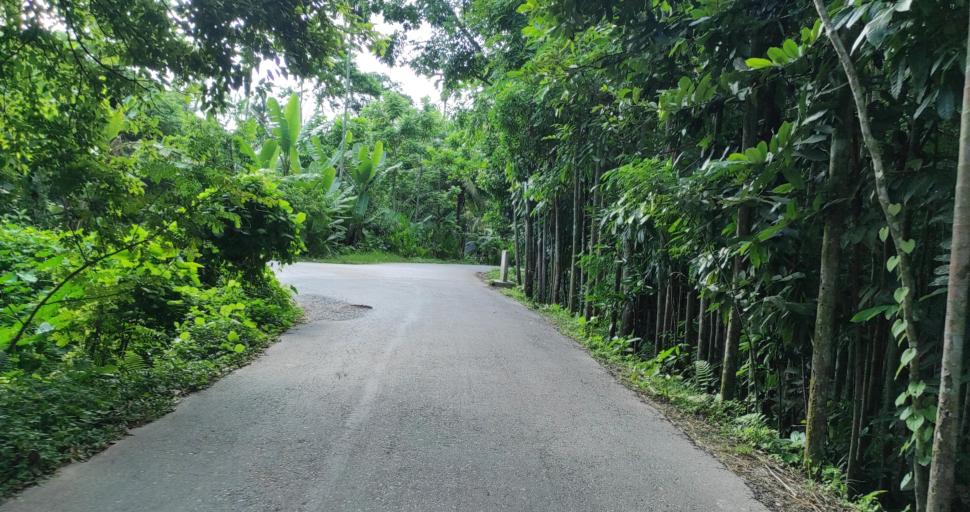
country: BD
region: Barisal
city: Gaurnadi
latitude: 22.8932
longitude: 90.1879
